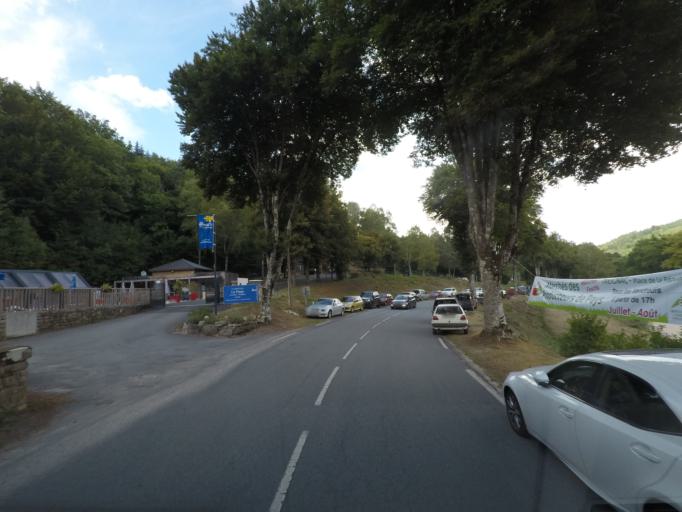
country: FR
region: Limousin
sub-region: Departement de la Correze
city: Treignac
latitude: 45.5596
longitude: 1.8135
